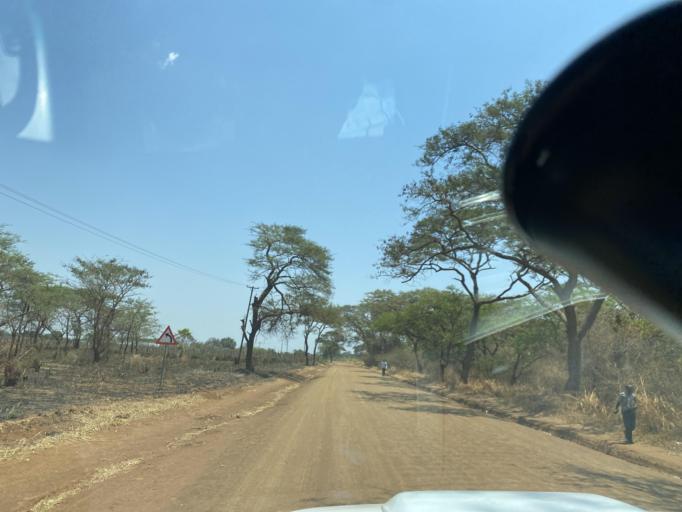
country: ZM
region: Lusaka
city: Lusaka
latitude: -15.4194
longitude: 28.1037
